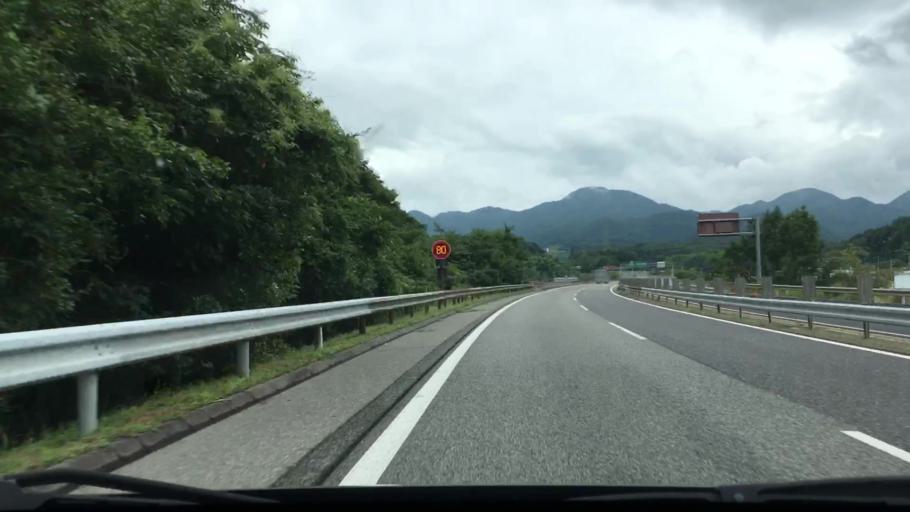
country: JP
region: Hiroshima
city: Hiroshima-shi
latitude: 34.6698
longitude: 132.5395
